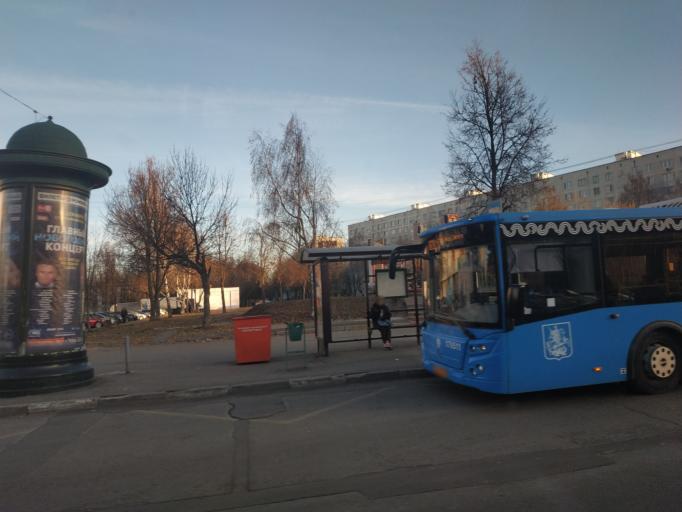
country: RU
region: Moscow
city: Chertanovo Yuzhnoye
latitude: 55.6005
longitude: 37.6080
